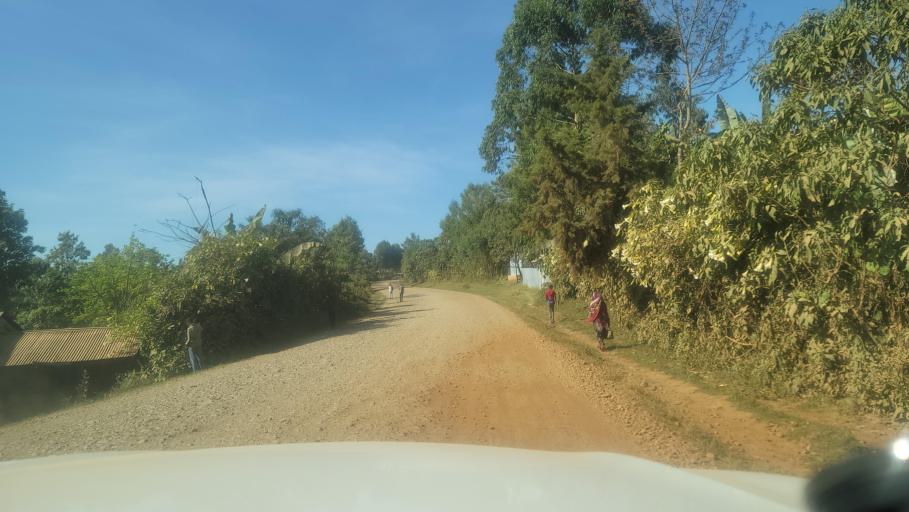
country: ET
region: Oromiya
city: Agaro
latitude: 7.7986
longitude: 36.4965
